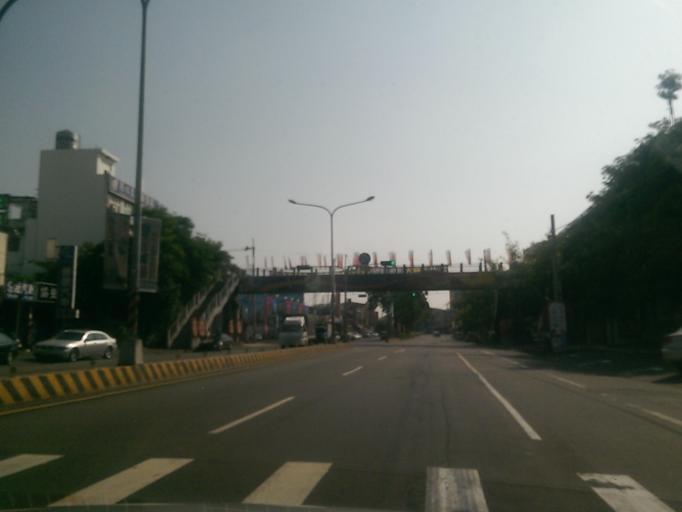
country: TW
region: Taiwan
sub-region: Changhua
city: Chang-hua
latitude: 24.0586
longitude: 120.5344
